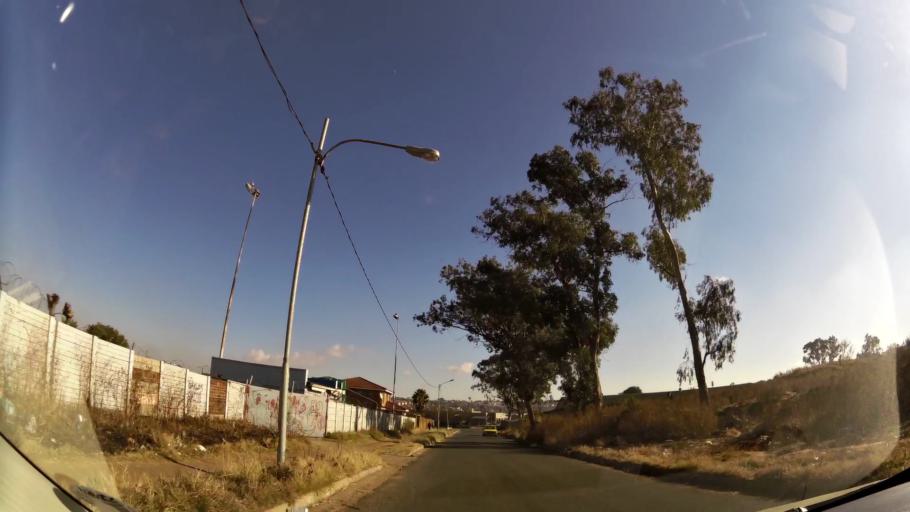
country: ZA
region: Gauteng
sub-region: City of Johannesburg Metropolitan Municipality
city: Roodepoort
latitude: -26.1549
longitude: 27.8549
